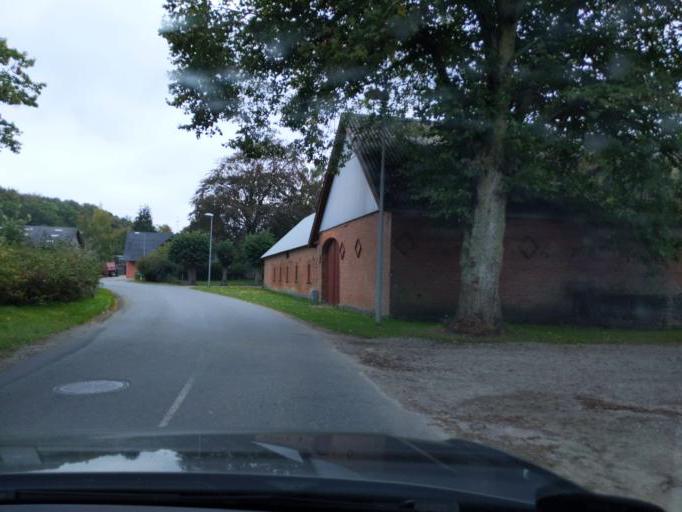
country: DK
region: North Denmark
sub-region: Mariagerfjord Kommune
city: Hobro
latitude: 56.5614
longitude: 9.6859
